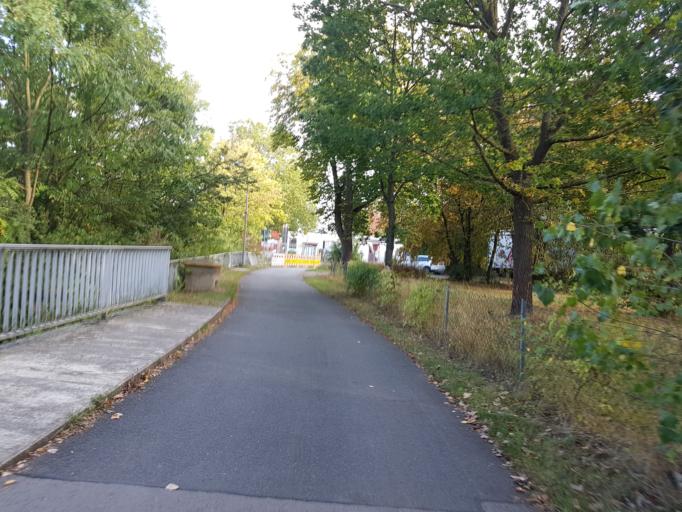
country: DE
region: Lower Saxony
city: Laatzen
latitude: 52.3616
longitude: 9.8624
